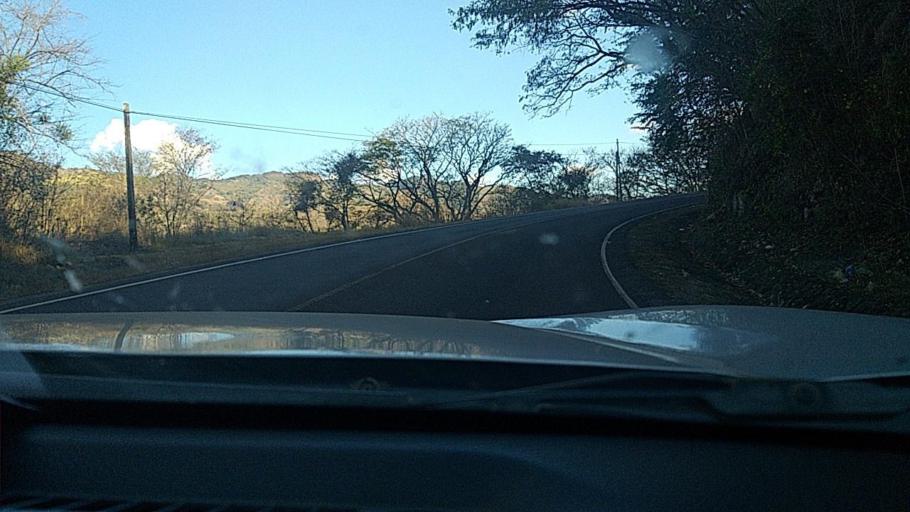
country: NI
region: Esteli
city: Condega
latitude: 13.2568
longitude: -86.3529
